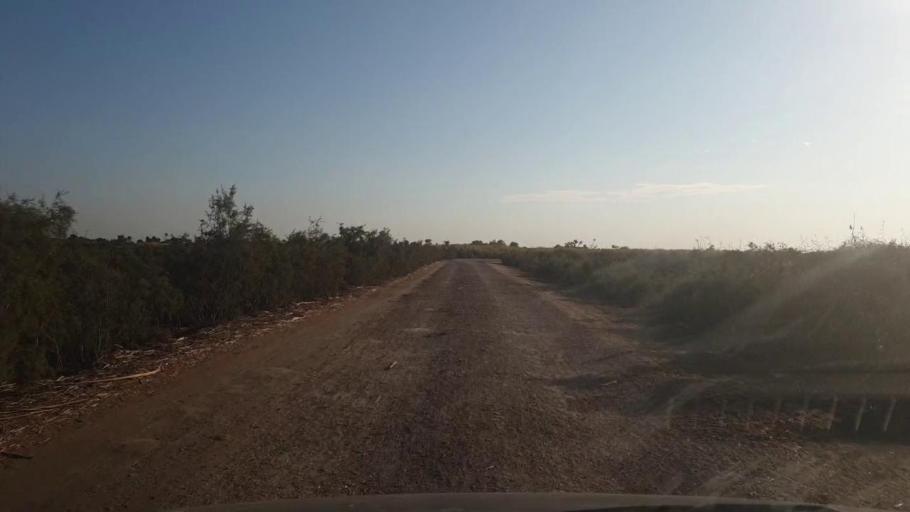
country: PK
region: Sindh
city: Sinjhoro
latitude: 26.0500
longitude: 68.8708
